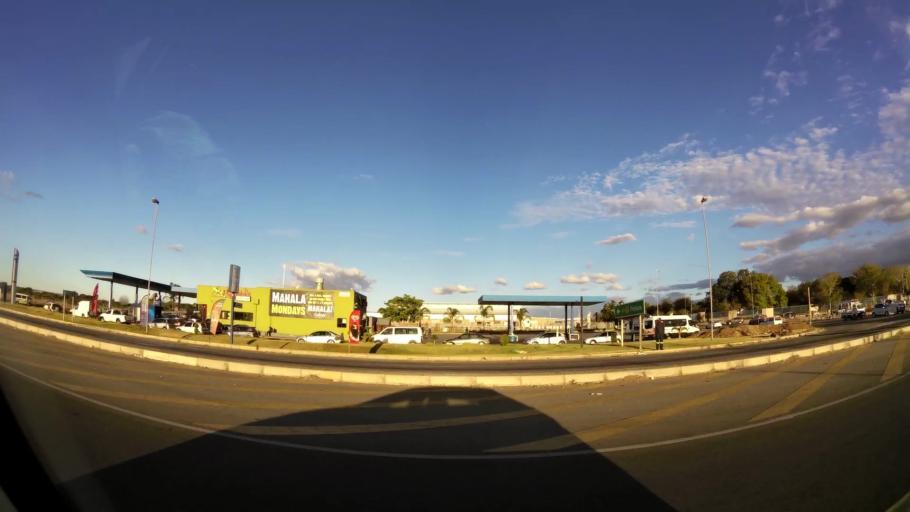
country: ZA
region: Limpopo
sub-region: Capricorn District Municipality
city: Polokwane
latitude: -23.8607
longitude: 29.4711
